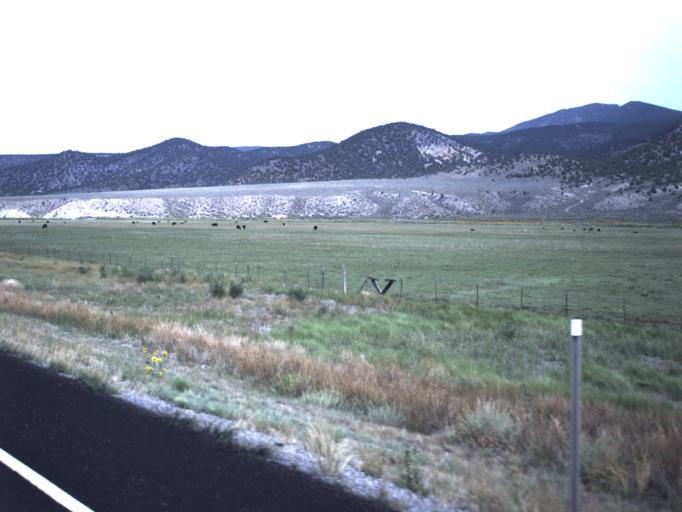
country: US
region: Utah
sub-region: Garfield County
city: Panguitch
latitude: 38.0387
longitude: -112.3554
